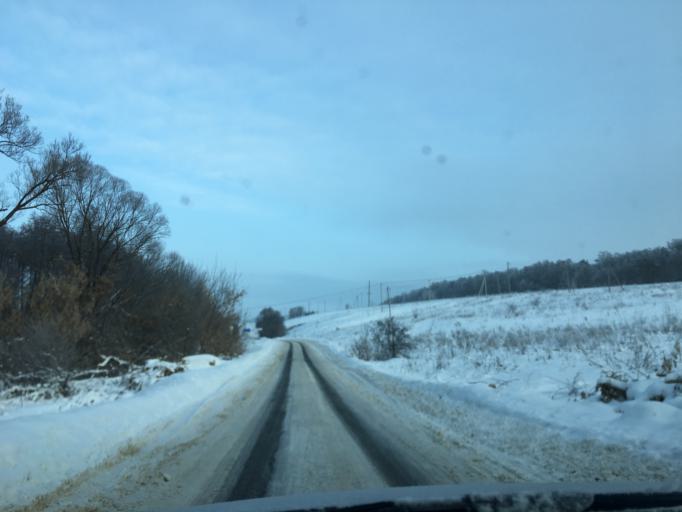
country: RU
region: Belgorod
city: Severnyy
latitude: 50.7255
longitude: 36.6116
